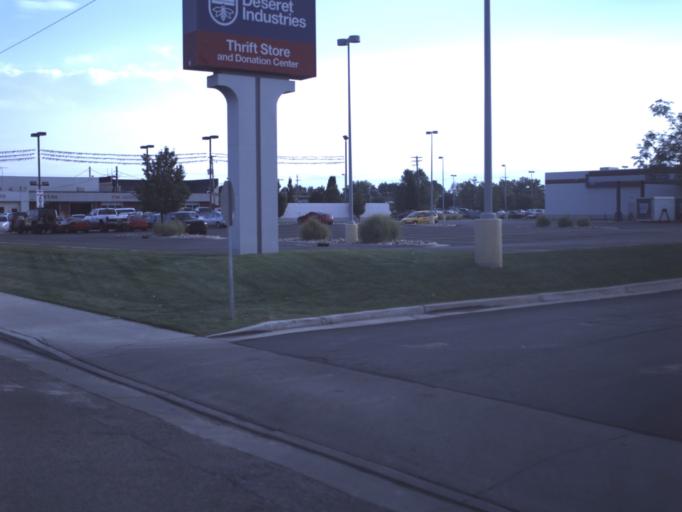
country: US
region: Utah
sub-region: Salt Lake County
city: Murray
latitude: 40.6761
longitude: -111.8884
